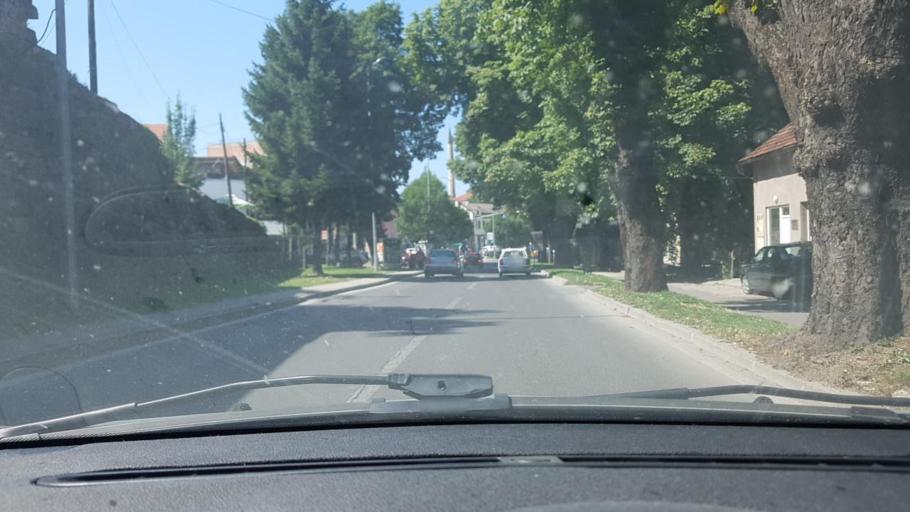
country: BA
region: Federation of Bosnia and Herzegovina
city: Bihac
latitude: 44.8140
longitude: 15.8708
